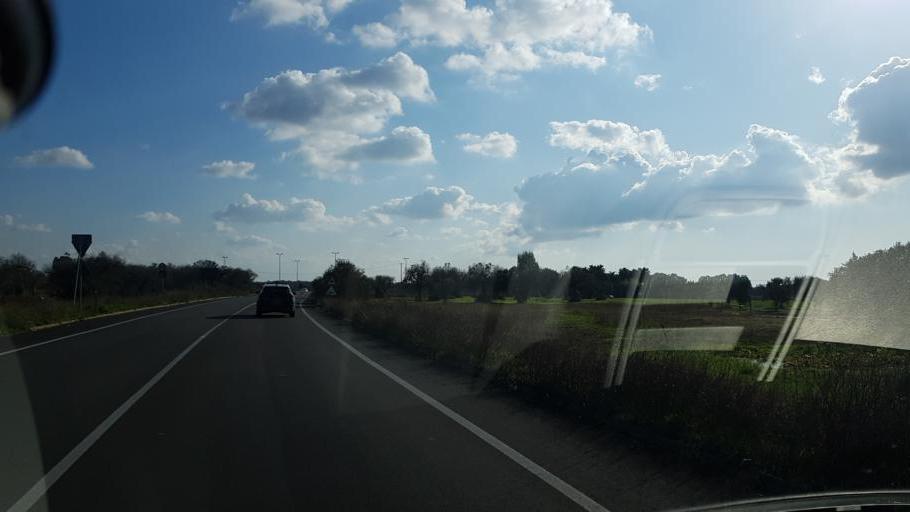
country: IT
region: Apulia
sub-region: Provincia di Lecce
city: Veglie
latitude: 40.3379
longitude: 17.9808
